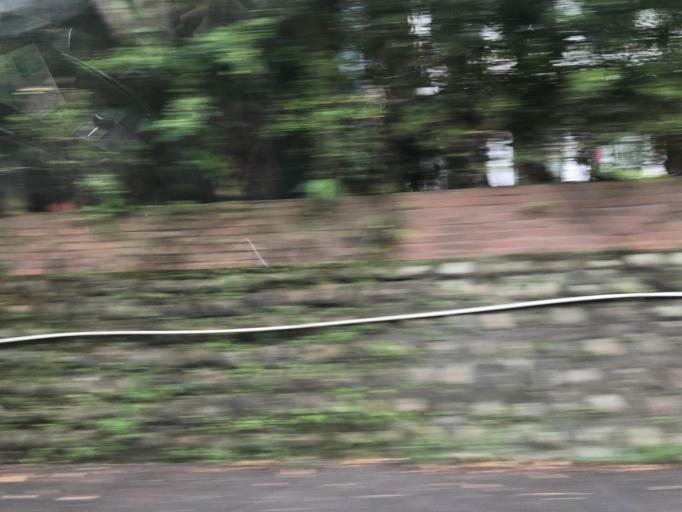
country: TW
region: Taiwan
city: Daxi
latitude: 24.9123
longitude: 121.3881
